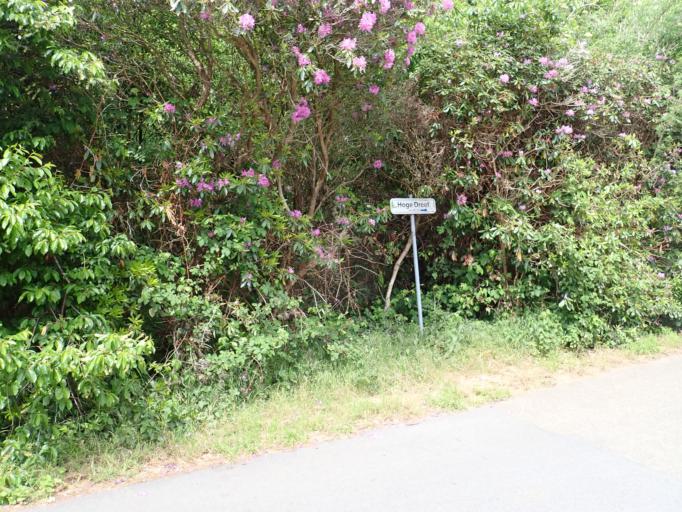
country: BE
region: Flanders
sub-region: Provincie Antwerpen
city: Westerlo
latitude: 51.0770
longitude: 4.9186
